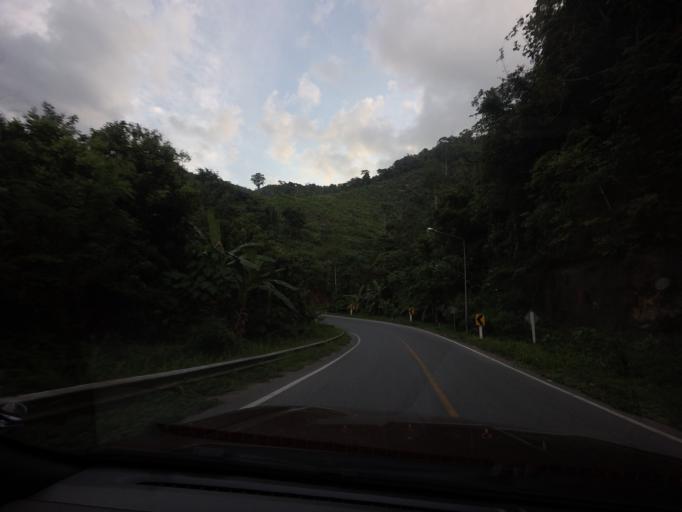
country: TH
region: Yala
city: Than To
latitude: 6.0103
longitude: 101.1954
